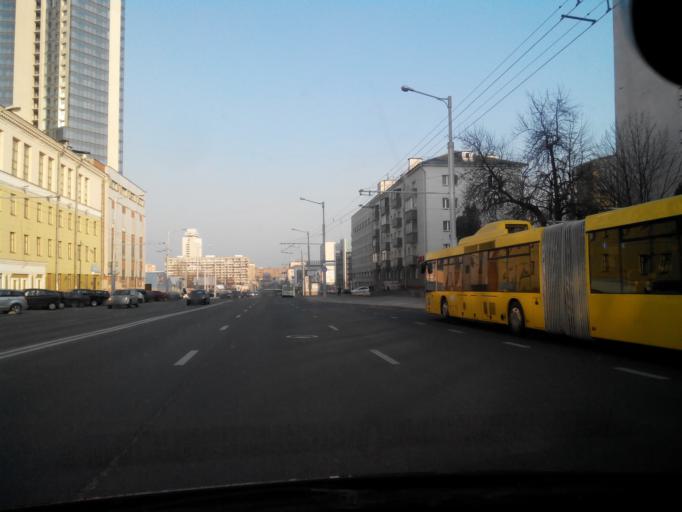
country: BY
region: Minsk
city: Minsk
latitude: 53.9063
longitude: 27.5294
